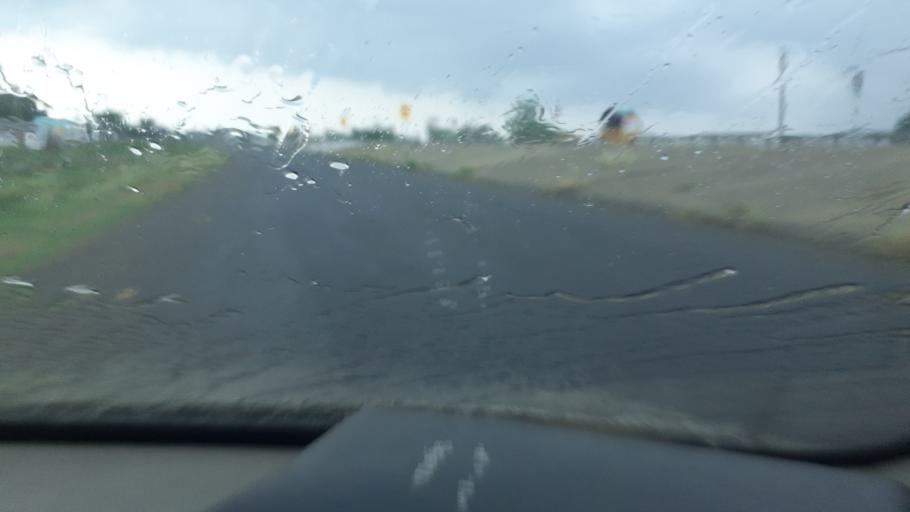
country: IN
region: Tamil Nadu
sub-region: Thoothukkudi
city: Kovilpatti
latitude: 9.0984
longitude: 77.8067
